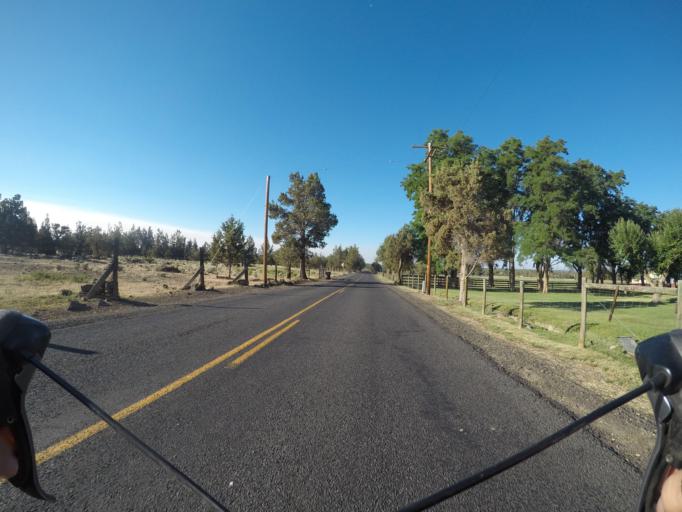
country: US
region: Oregon
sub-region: Deschutes County
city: Redmond
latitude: 44.2723
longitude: -121.2507
